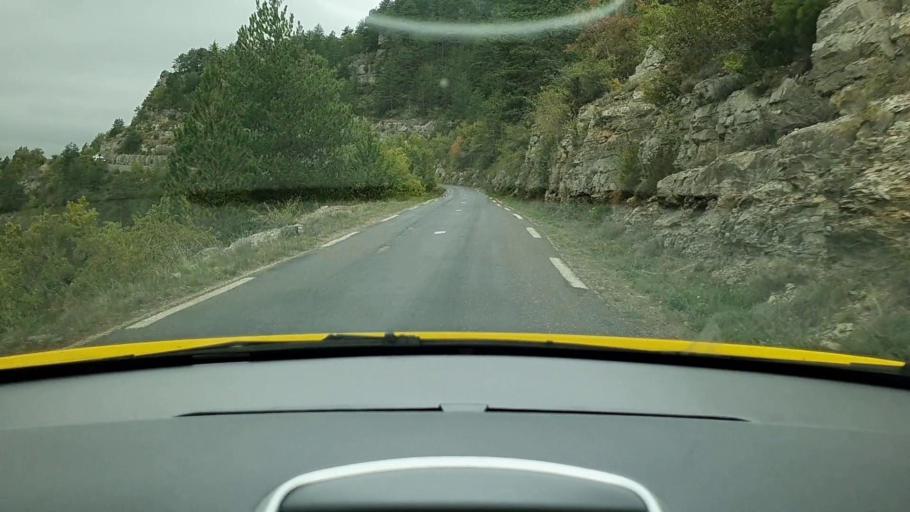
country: FR
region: Languedoc-Roussillon
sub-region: Departement de la Lozere
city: Meyrueis
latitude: 44.0783
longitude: 3.3637
